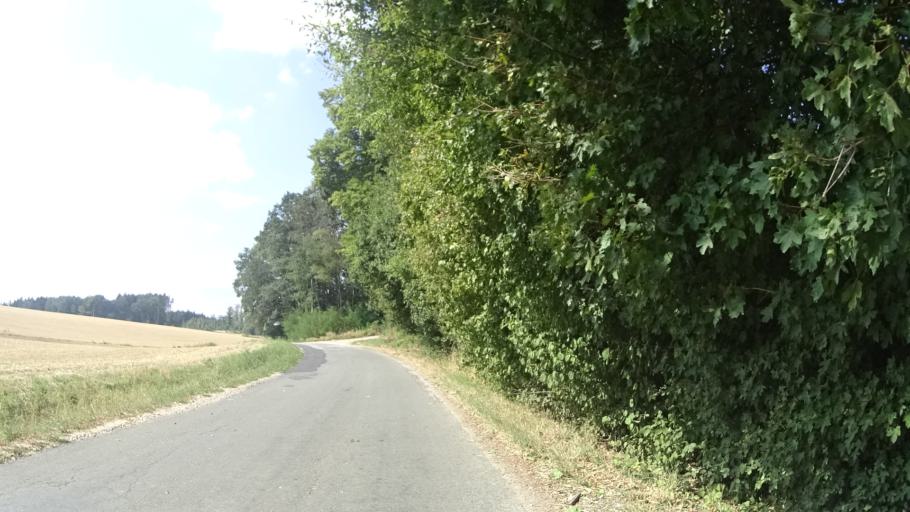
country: CZ
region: Kralovehradecky
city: Liban
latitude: 50.4254
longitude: 15.2616
